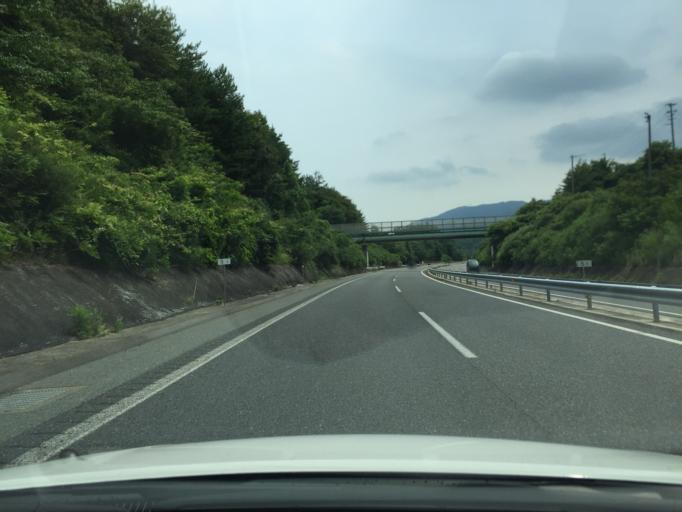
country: JP
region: Fukushima
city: Iwaki
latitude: 37.0773
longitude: 140.7910
